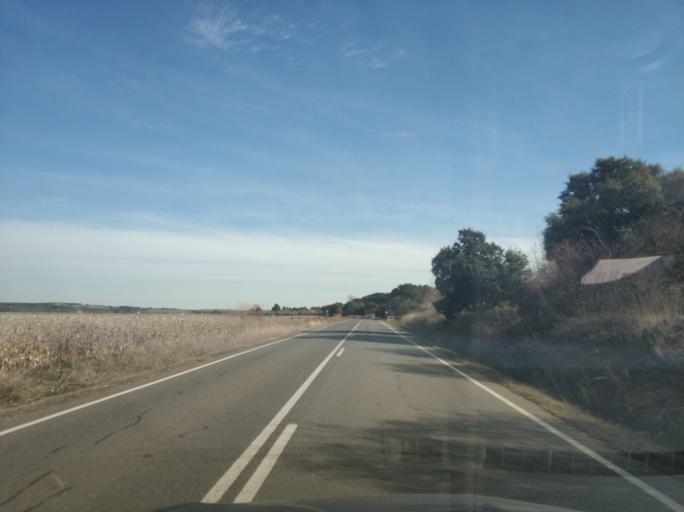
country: ES
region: Castille and Leon
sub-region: Provincia de Salamanca
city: Valverdon
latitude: 41.0370
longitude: -5.7773
